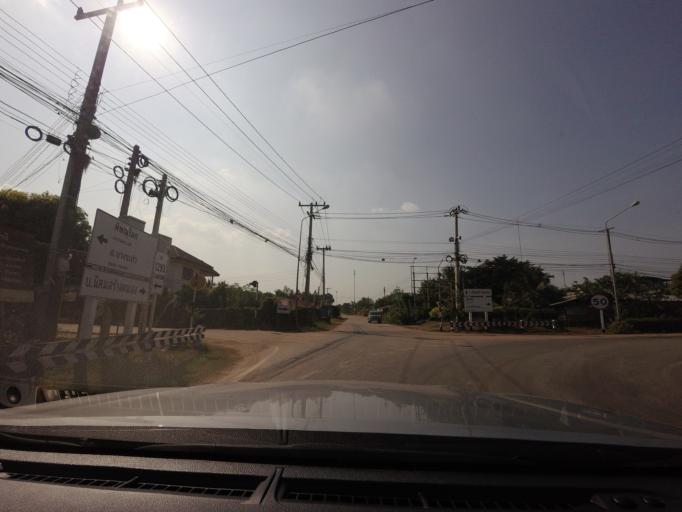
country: TH
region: Sukhothai
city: Kong Krailat
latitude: 16.8147
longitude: 99.9759
